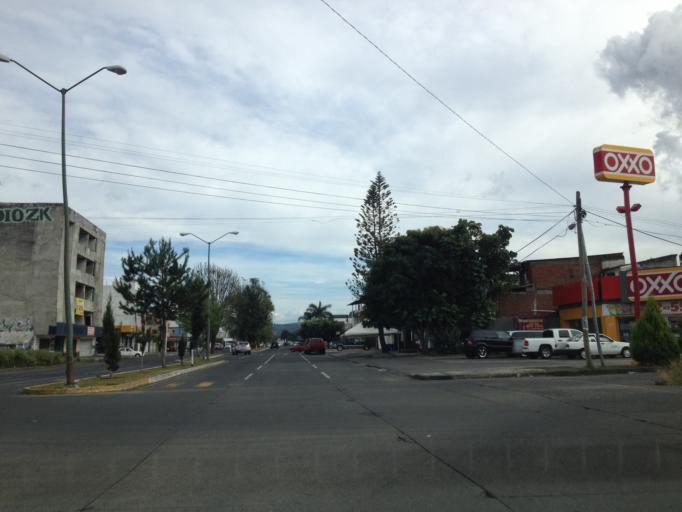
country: MX
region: Michoacan
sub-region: Uruapan
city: Uruapan
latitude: 19.4036
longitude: -102.0457
